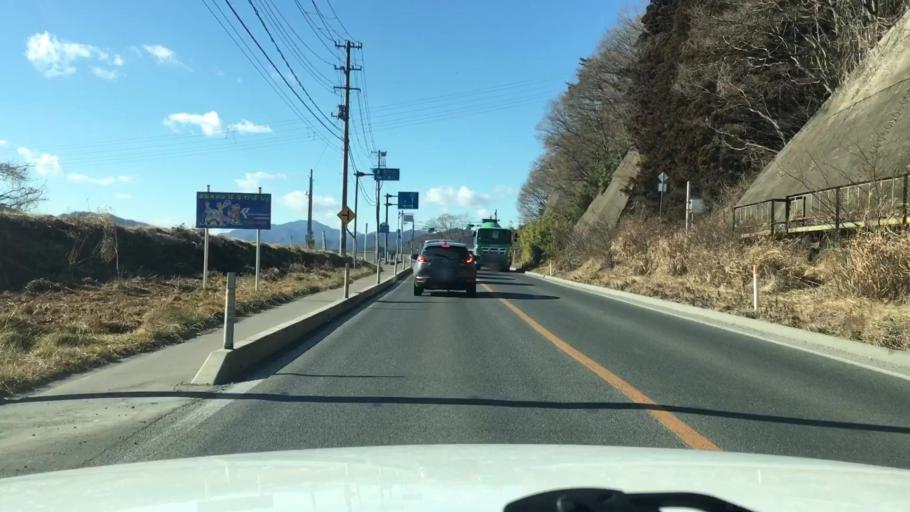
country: JP
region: Iwate
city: Miyako
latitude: 39.6312
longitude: 141.9079
